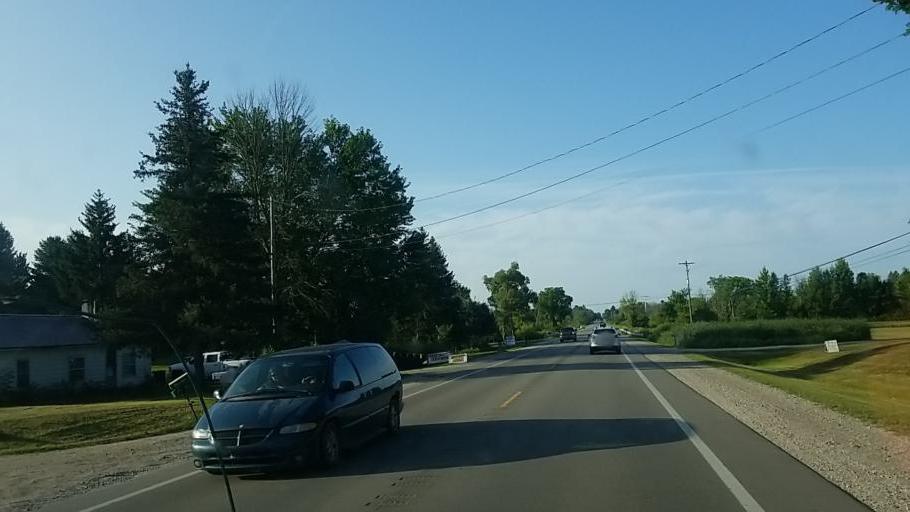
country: US
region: Michigan
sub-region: Montcalm County
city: Stanton
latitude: 43.2272
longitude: -85.0736
